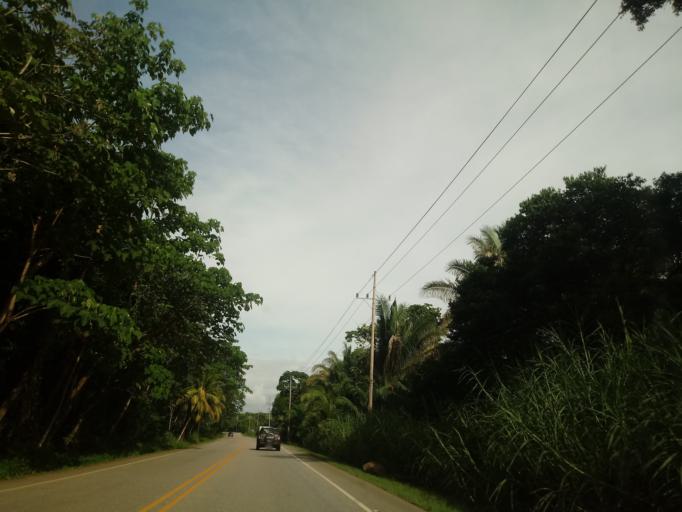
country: CR
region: San Jose
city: Daniel Flores
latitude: 9.1935
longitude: -83.7790
